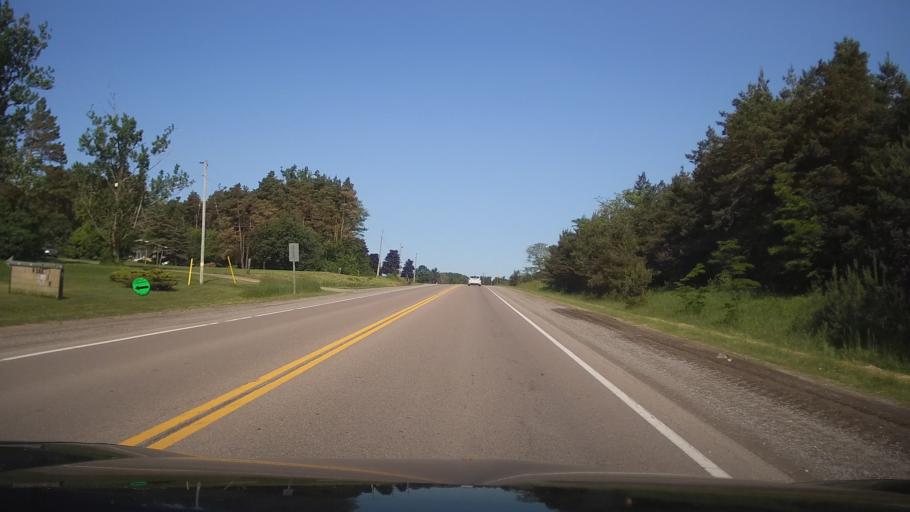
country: CA
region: Ontario
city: Omemee
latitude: 44.3474
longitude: -78.7803
